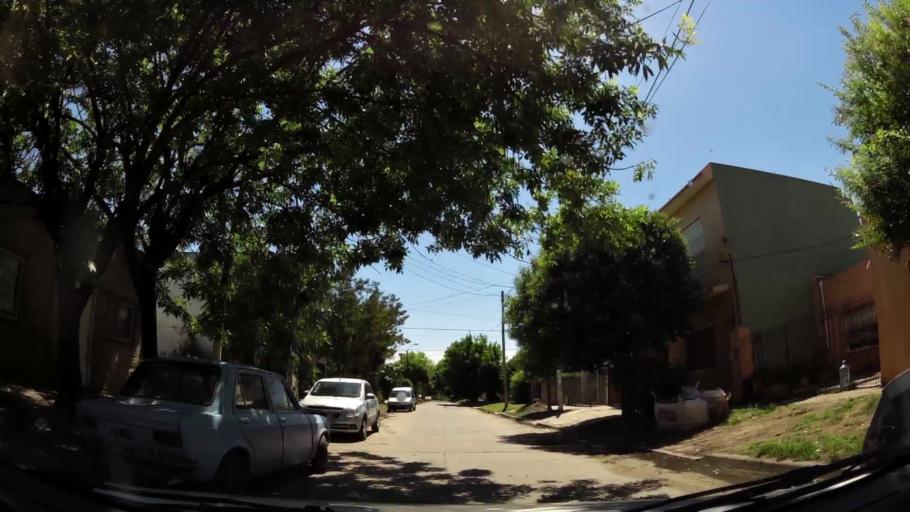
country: AR
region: Buenos Aires
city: Ituzaingo
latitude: -34.6746
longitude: -58.6705
